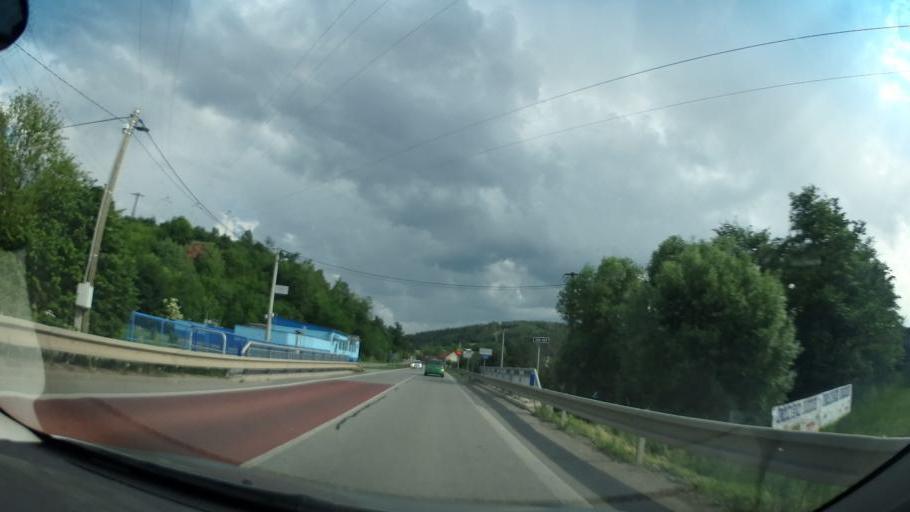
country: CZ
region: South Moravian
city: Tisnov
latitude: 49.3317
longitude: 16.4391
